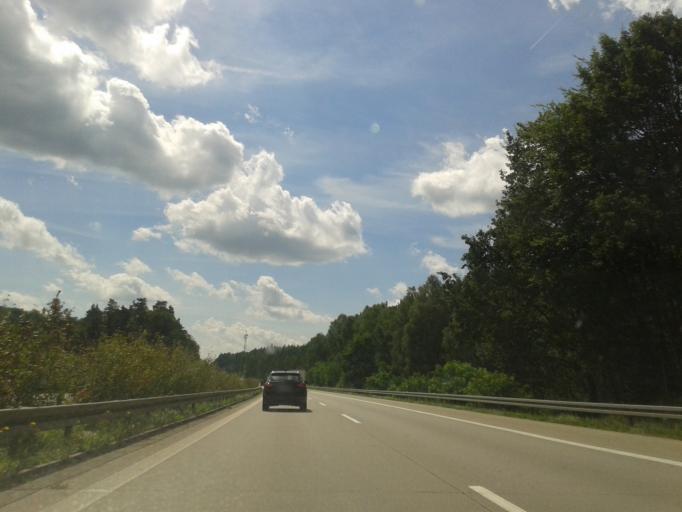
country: DE
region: Brandenburg
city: Wandlitz
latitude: 52.7552
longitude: 13.5436
